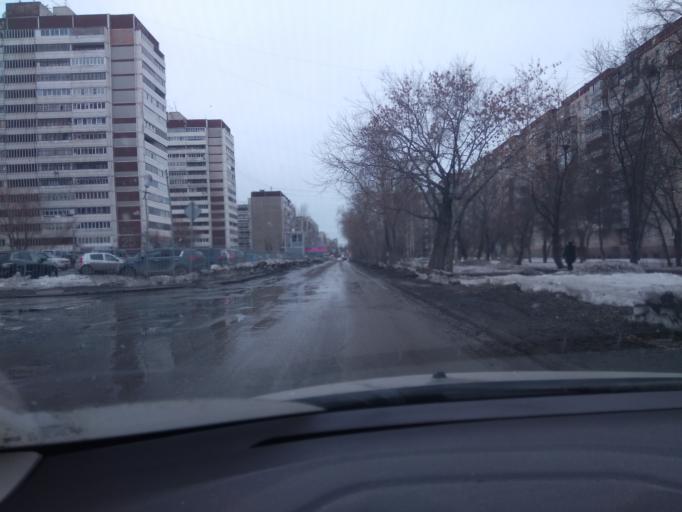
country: RU
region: Sverdlovsk
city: Yekaterinburg
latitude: 56.8925
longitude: 60.6078
